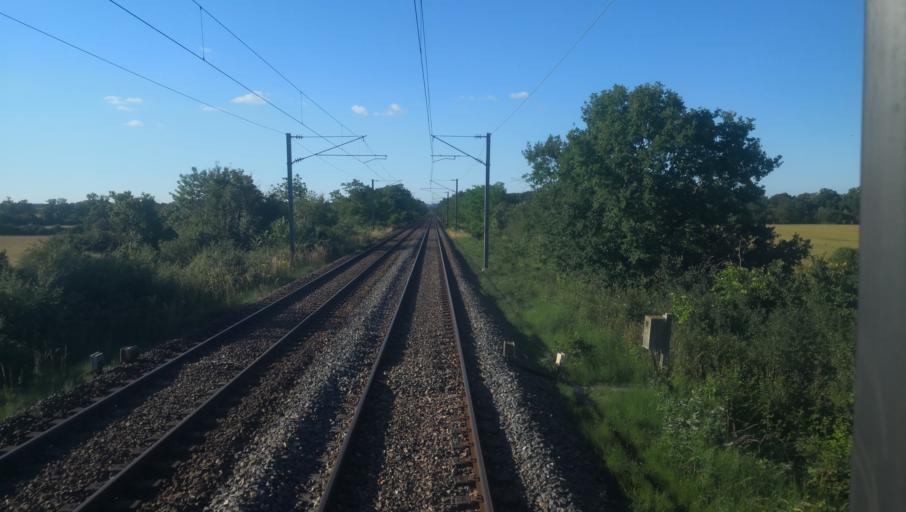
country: FR
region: Bourgogne
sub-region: Departement de la Nievre
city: Saint-Pierre-le-Moutier
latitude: 46.8375
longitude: 3.1169
